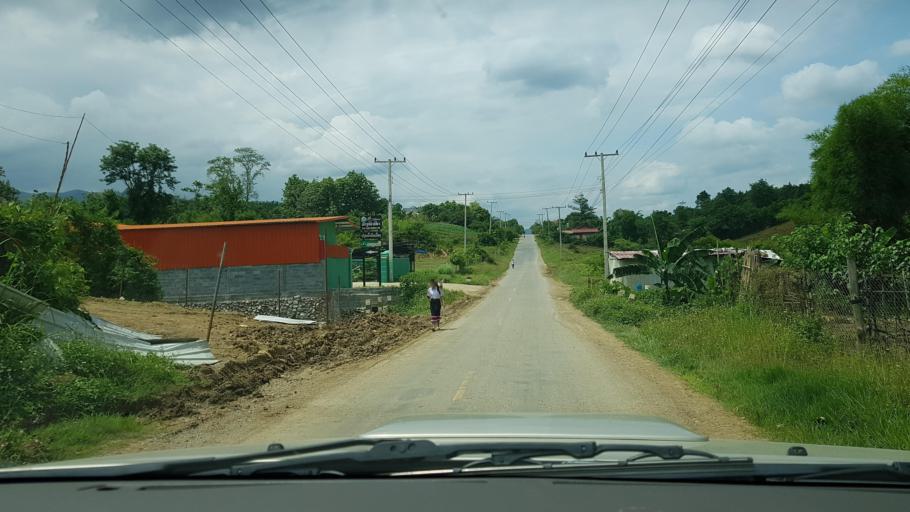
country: LA
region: Loungnamtha
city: Muang Nale
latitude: 20.0349
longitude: 101.3471
